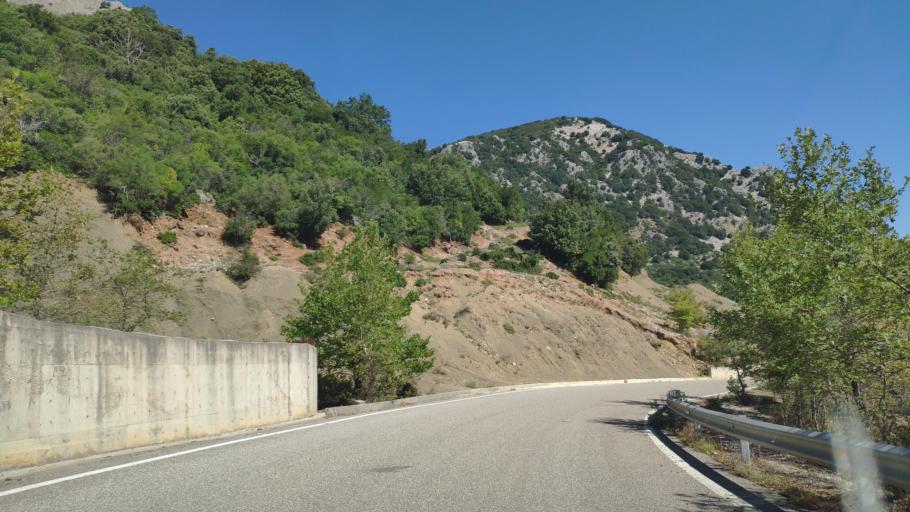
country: GR
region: Central Greece
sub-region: Nomos Evrytanias
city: Kerasochori
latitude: 38.9414
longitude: 21.4580
